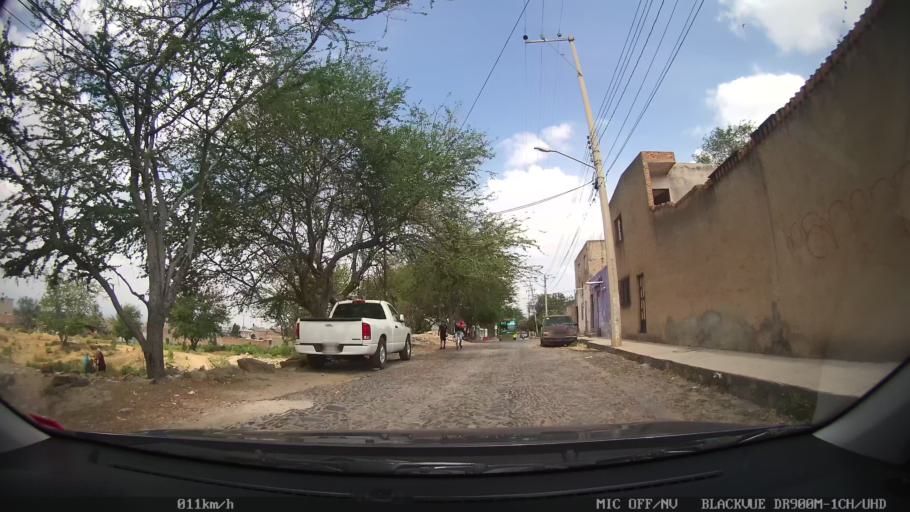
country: MX
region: Jalisco
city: Tonala
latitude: 20.6298
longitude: -103.2293
